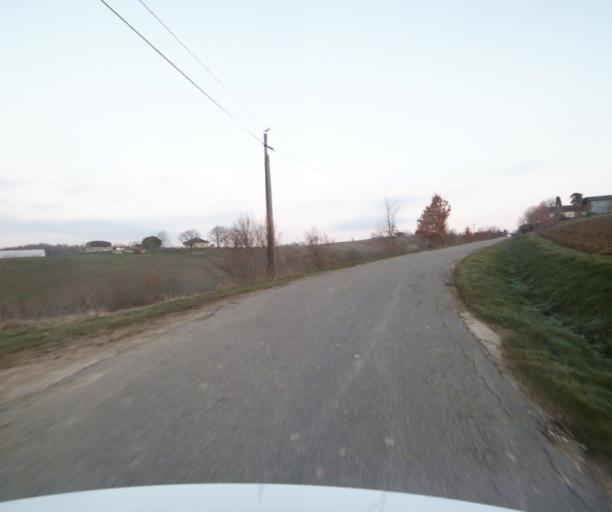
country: FR
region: Midi-Pyrenees
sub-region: Departement du Tarn-et-Garonne
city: Moissac
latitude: 44.1235
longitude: 1.0508
